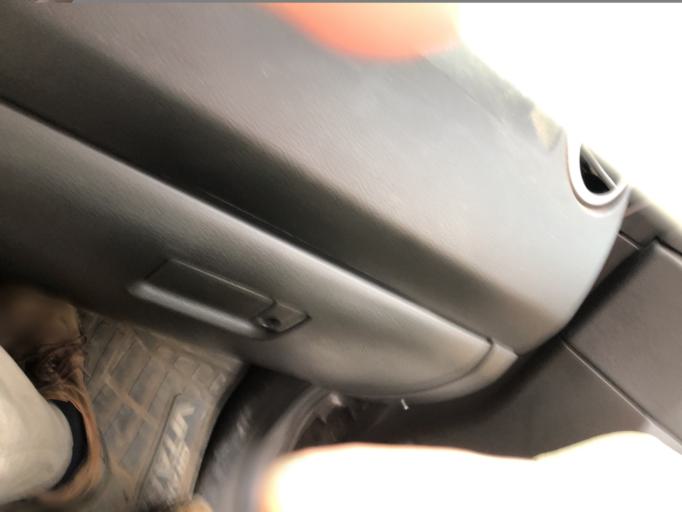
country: EC
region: Imbabura
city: Ibarra
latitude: 0.3544
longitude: -78.1399
